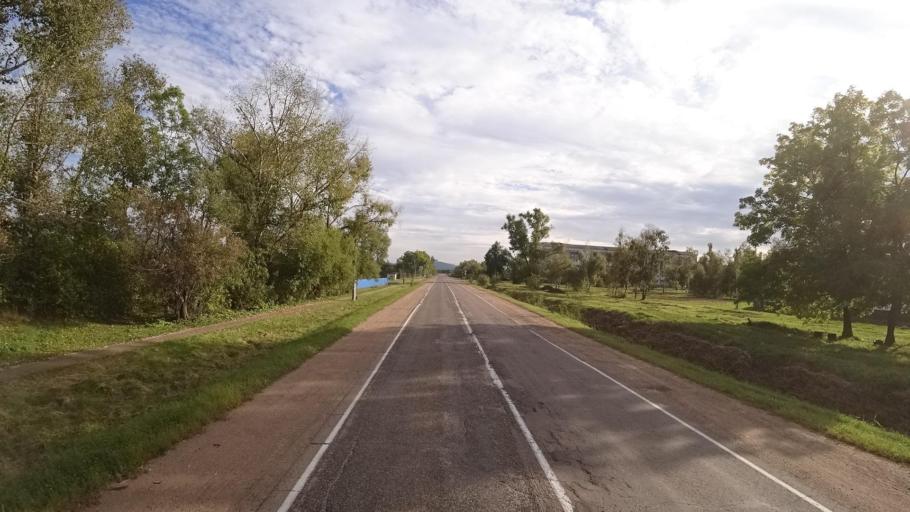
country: RU
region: Primorskiy
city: Dostoyevka
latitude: 44.2908
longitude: 133.4264
